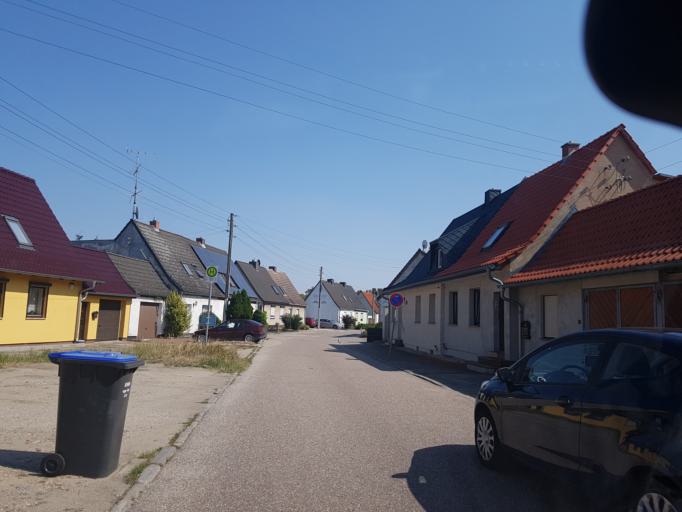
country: DE
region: Saxony-Anhalt
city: Coswig
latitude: 51.8973
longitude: 12.4639
